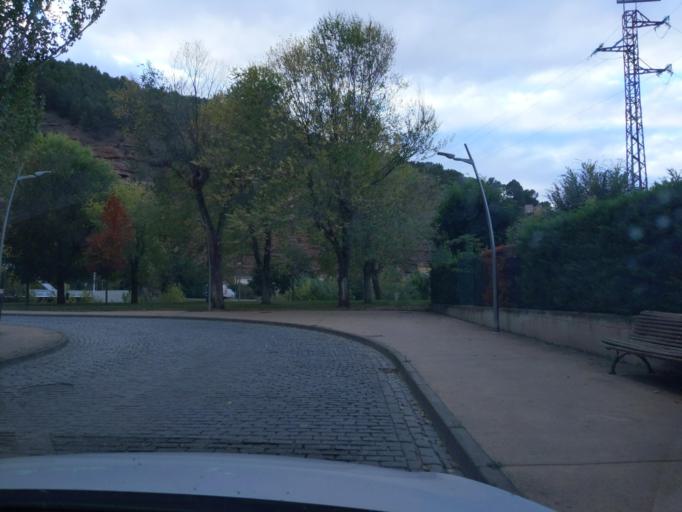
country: ES
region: La Rioja
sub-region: Provincia de La Rioja
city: Najera
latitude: 42.4135
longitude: -2.7325
